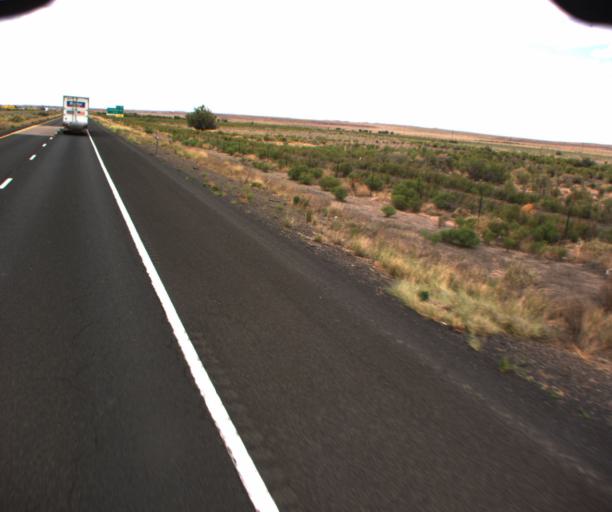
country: US
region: Arizona
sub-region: Navajo County
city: Joseph City
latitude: 34.9668
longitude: -110.4172
